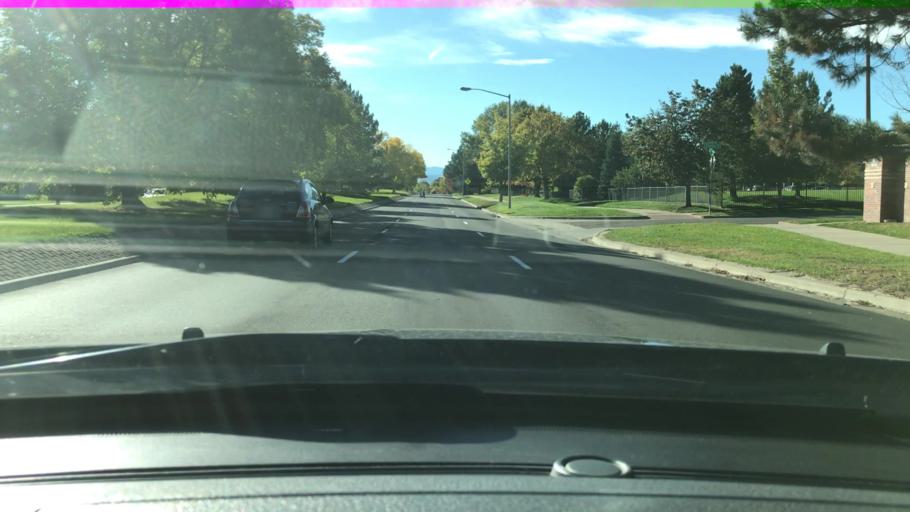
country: US
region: Colorado
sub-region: Arapahoe County
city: Glendale
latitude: 39.7114
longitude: -104.9070
